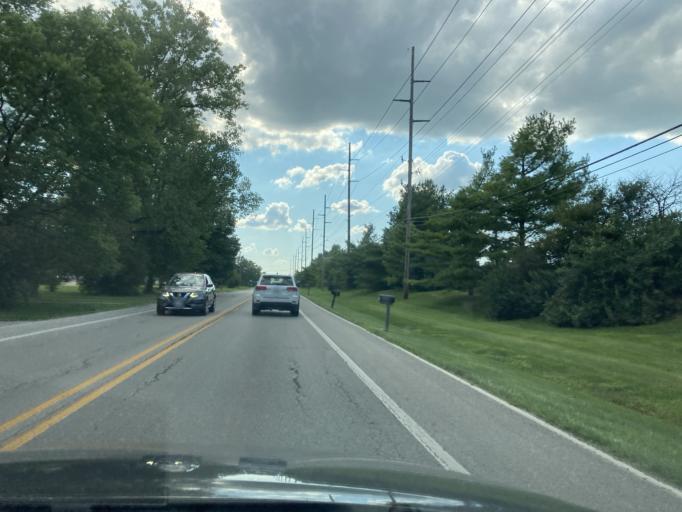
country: US
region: Indiana
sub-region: Marion County
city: Speedway
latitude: 39.8536
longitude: -86.2205
